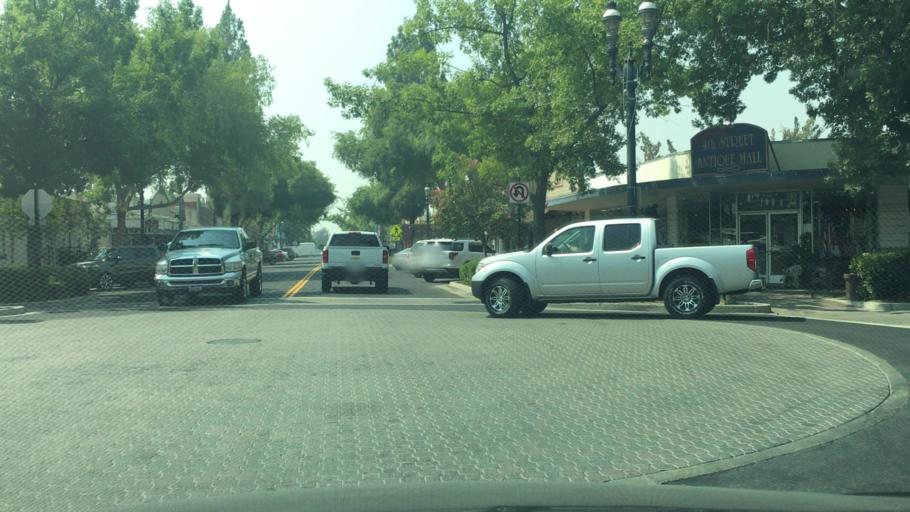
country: US
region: California
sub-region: Fresno County
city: Clovis
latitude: 36.8254
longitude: -119.7021
